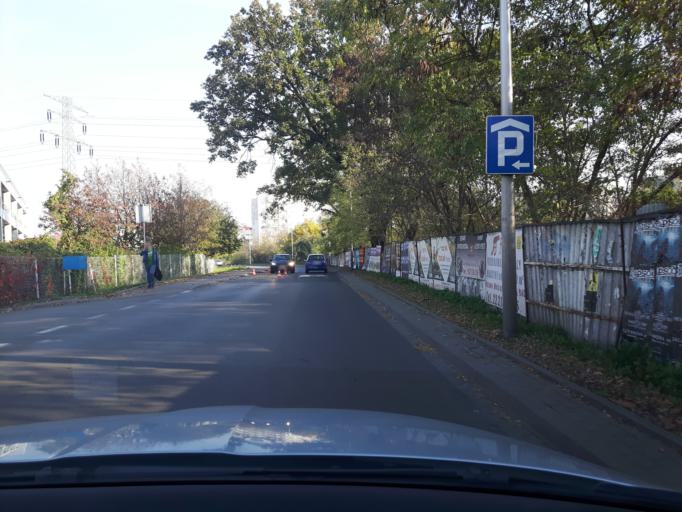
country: PL
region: Masovian Voivodeship
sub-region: Warszawa
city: Ochota
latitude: 52.2114
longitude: 20.9580
